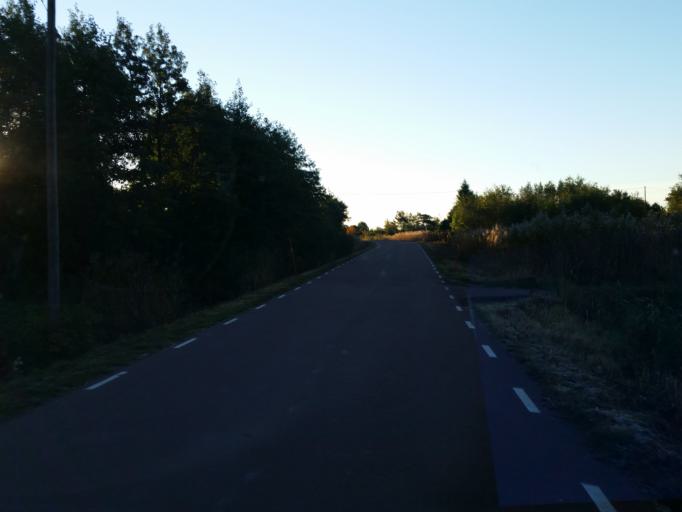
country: AX
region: Alands skaergard
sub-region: Vardoe
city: Vardoe
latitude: 60.3407
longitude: 20.3562
